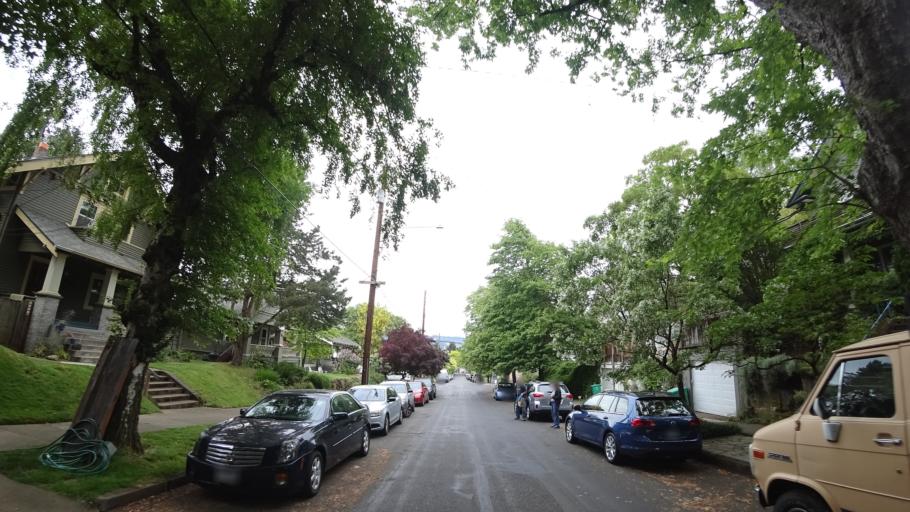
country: US
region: Oregon
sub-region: Multnomah County
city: Portland
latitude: 45.4998
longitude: -122.6368
